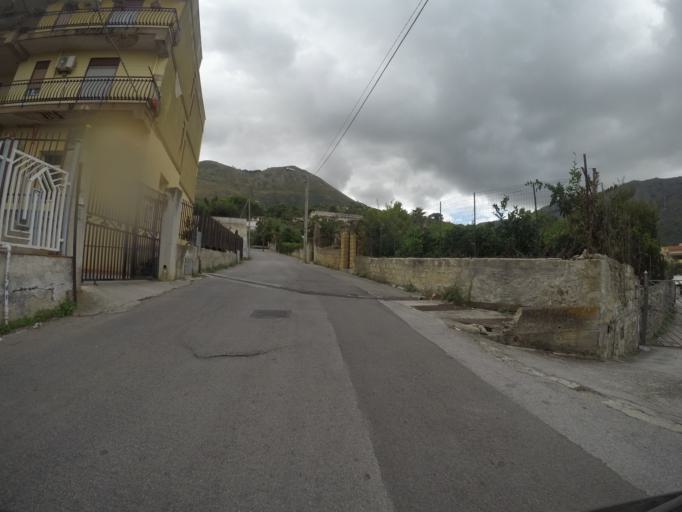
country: IT
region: Sicily
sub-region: Palermo
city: Carini
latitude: 38.1279
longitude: 13.1819
